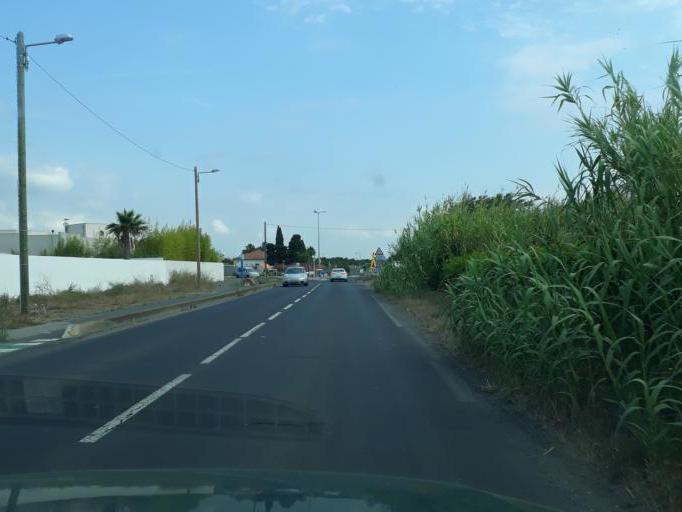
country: FR
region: Languedoc-Roussillon
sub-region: Departement de l'Herault
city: Agde
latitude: 43.2849
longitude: 3.4817
